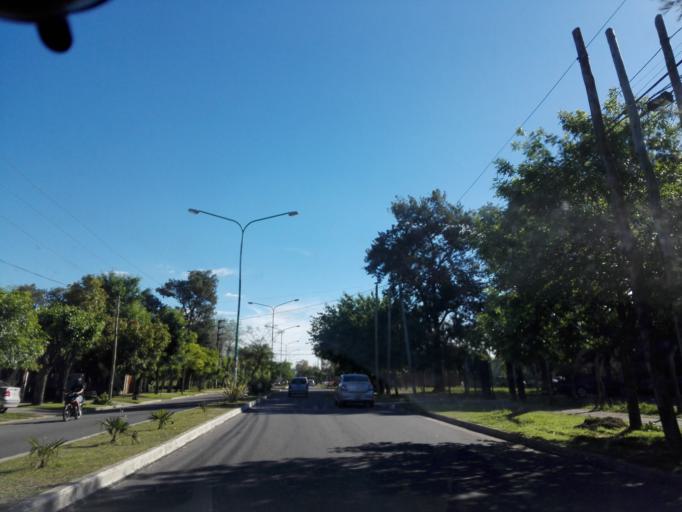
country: AR
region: Buenos Aires
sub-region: Partido de La Plata
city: La Plata
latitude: -34.8883
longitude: -58.0048
